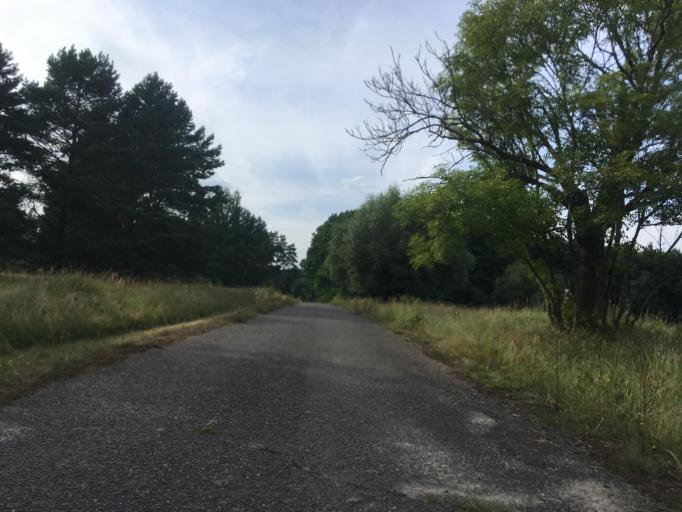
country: DE
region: Brandenburg
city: Eberswalde
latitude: 52.7847
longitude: 13.8273
